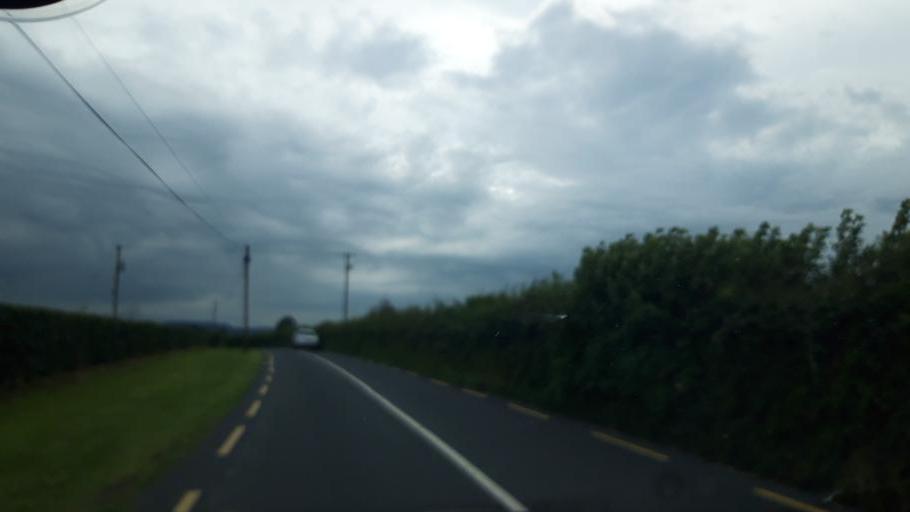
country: IE
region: Leinster
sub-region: Kilkenny
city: Ballyragget
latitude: 52.7479
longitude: -7.3920
